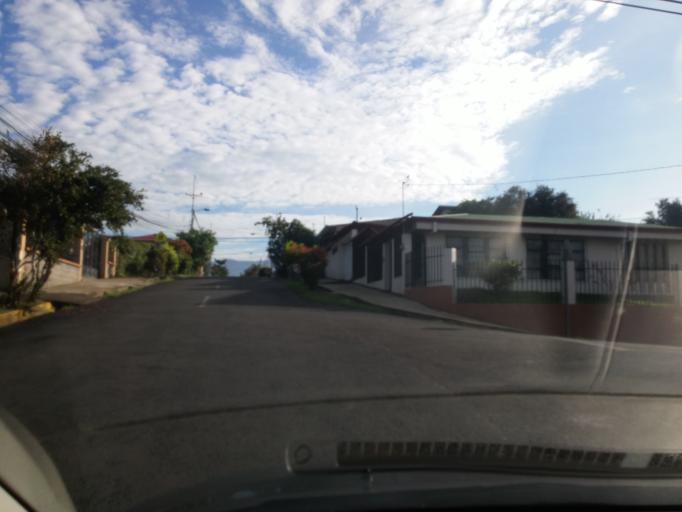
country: CR
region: Heredia
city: Llorente
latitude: 10.0012
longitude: -84.1504
